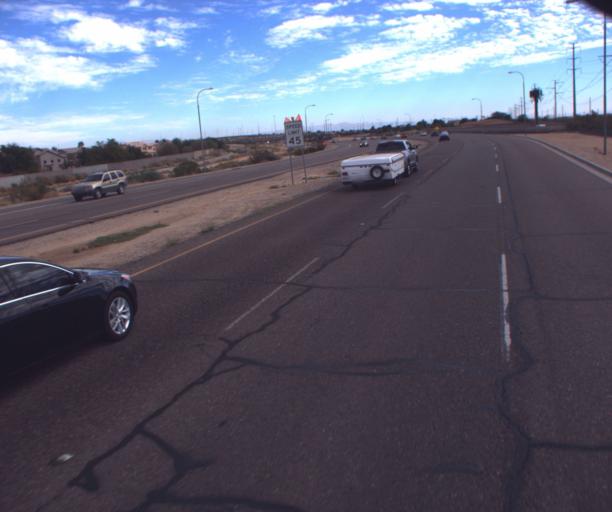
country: US
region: Arizona
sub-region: Maricopa County
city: Guadalupe
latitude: 33.2914
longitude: -111.9901
